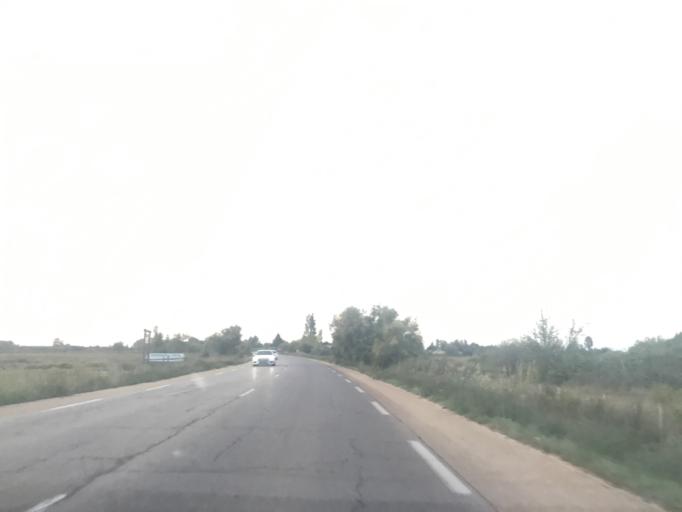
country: FR
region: Provence-Alpes-Cote d'Azur
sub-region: Departement des Bouches-du-Rhone
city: Saintes-Maries-de-la-Mer
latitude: 43.5208
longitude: 4.3996
